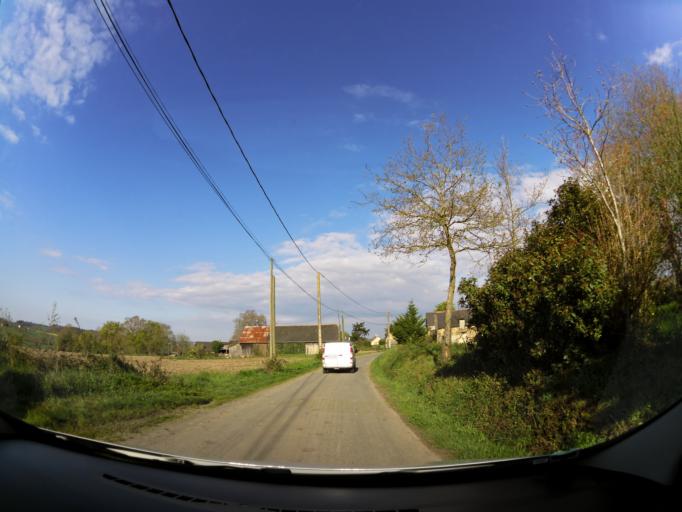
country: FR
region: Brittany
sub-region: Departement d'Ille-et-Vilaine
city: Crevin
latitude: 47.9395
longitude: -1.6811
